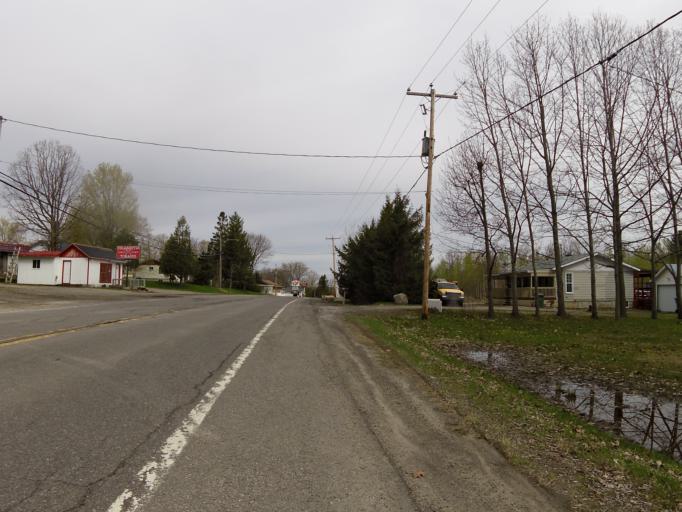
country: CA
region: Quebec
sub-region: Monteregie
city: Hudson
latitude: 45.5011
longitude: -74.1502
